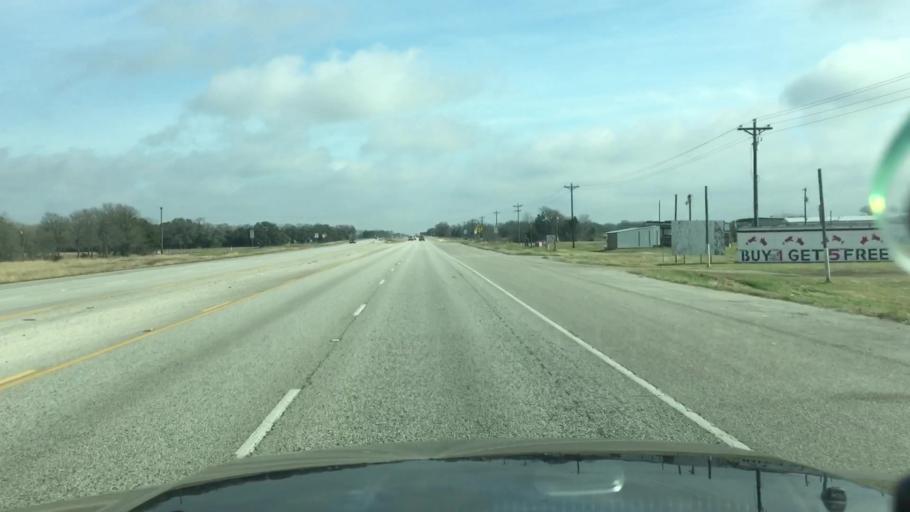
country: US
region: Texas
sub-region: Lee County
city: Giddings
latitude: 30.1753
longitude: -96.8912
